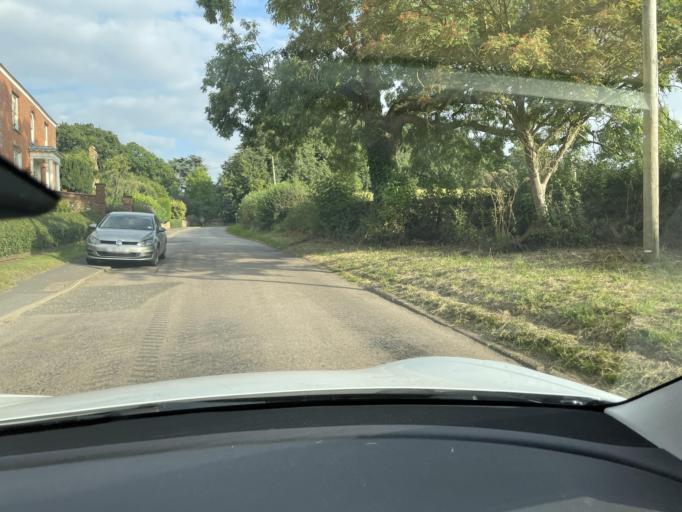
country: GB
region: England
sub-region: Northamptonshire
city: Brixworth
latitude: 52.3909
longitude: -0.9568
